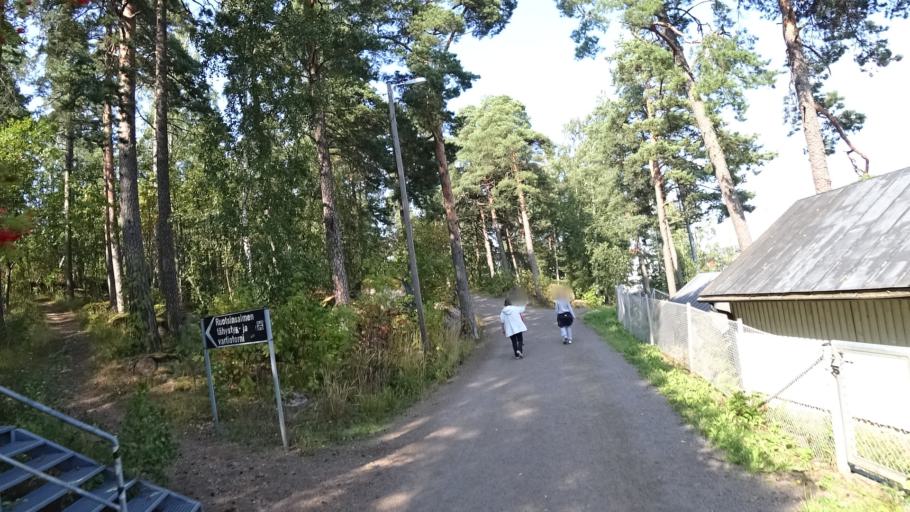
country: FI
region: Kymenlaakso
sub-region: Kotka-Hamina
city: Kotka
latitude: 60.4545
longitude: 26.9514
